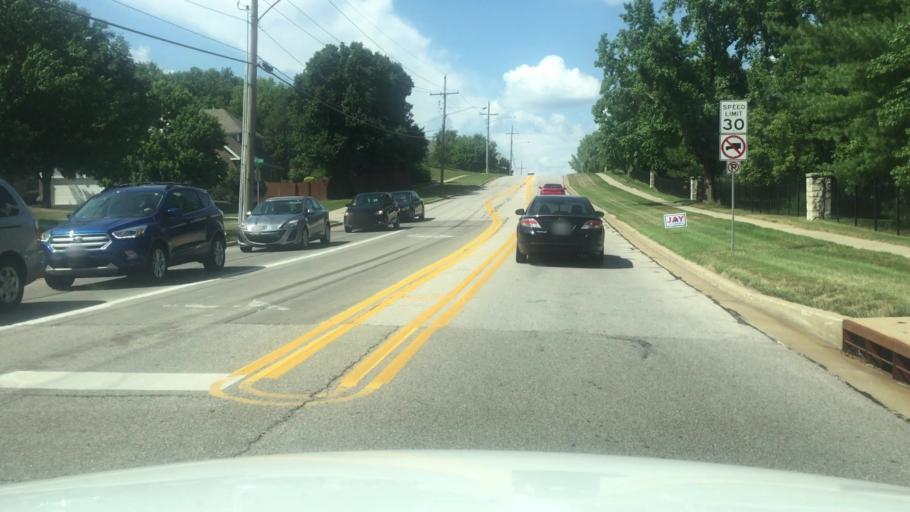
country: US
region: Kansas
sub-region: Johnson County
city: Lenexa
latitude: 38.9955
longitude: -94.7423
